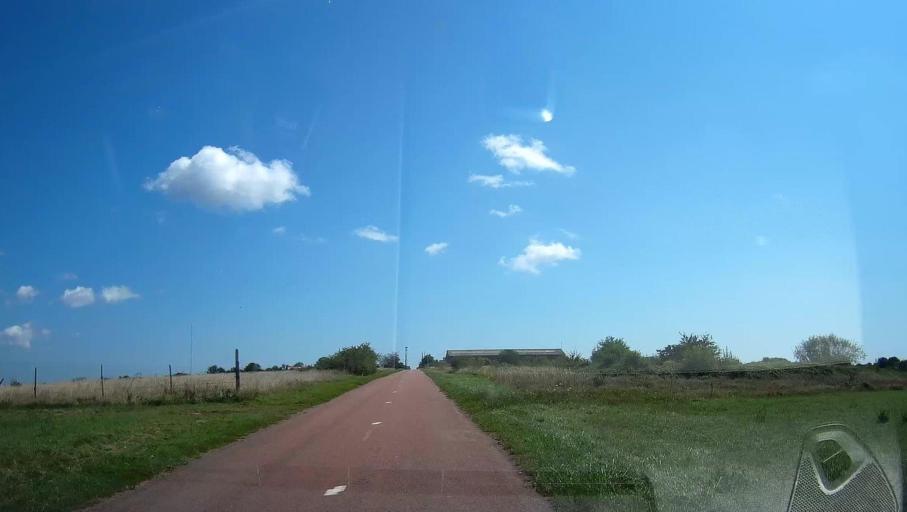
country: FR
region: Bourgogne
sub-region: Departement de la Cote-d'Or
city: Nolay
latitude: 46.9794
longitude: 4.6657
